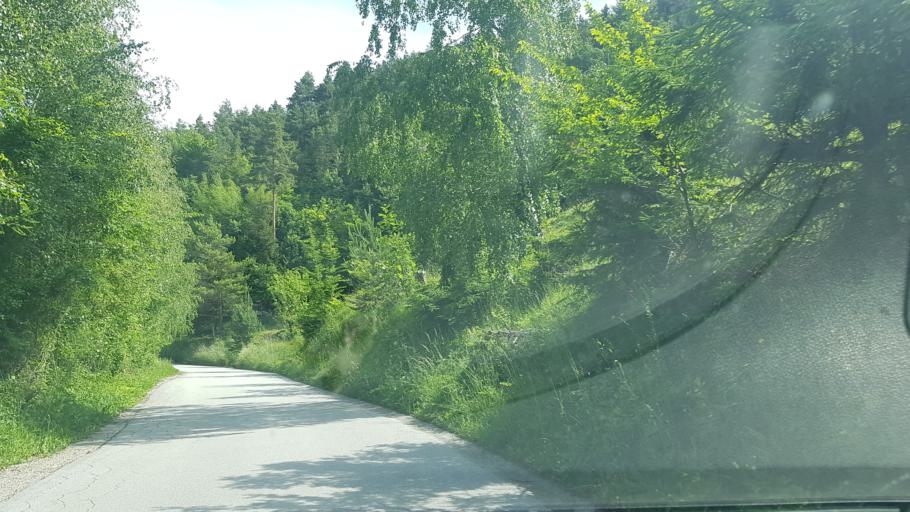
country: SI
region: Velenje
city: Velenje
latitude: 46.3830
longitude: 15.1735
